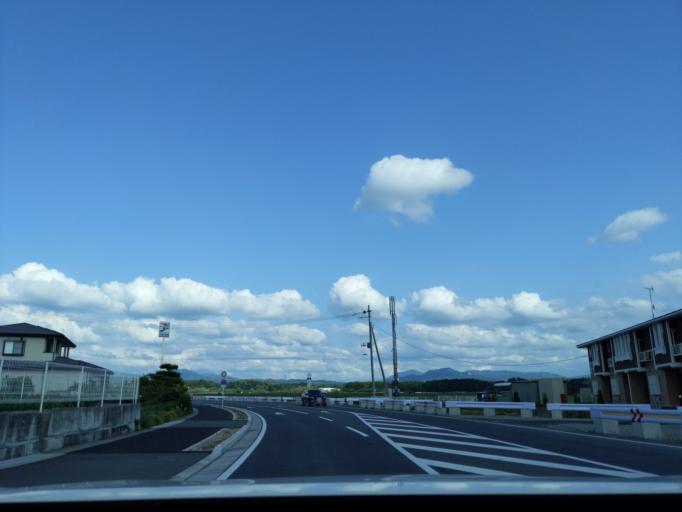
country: JP
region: Fukushima
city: Koriyama
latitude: 37.3544
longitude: 140.3808
